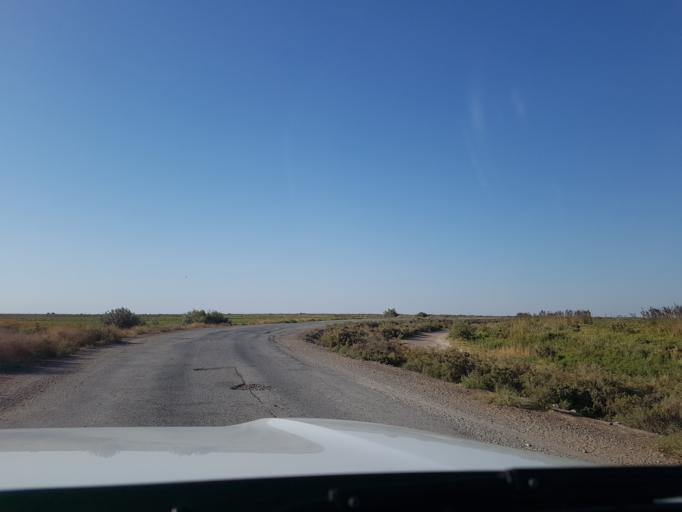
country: IR
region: Razavi Khorasan
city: Sarakhs
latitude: 36.9979
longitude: 61.3808
